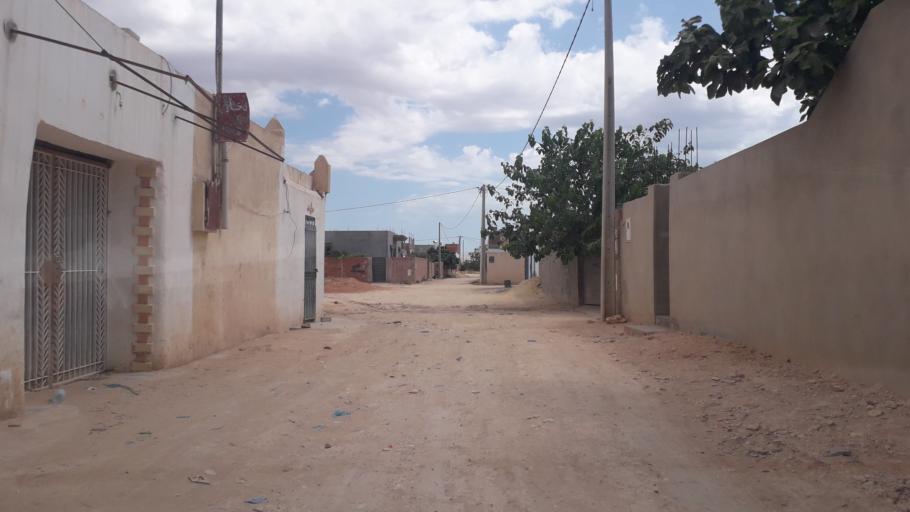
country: TN
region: Safaqis
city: Al Qarmadah
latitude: 34.8387
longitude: 10.7759
